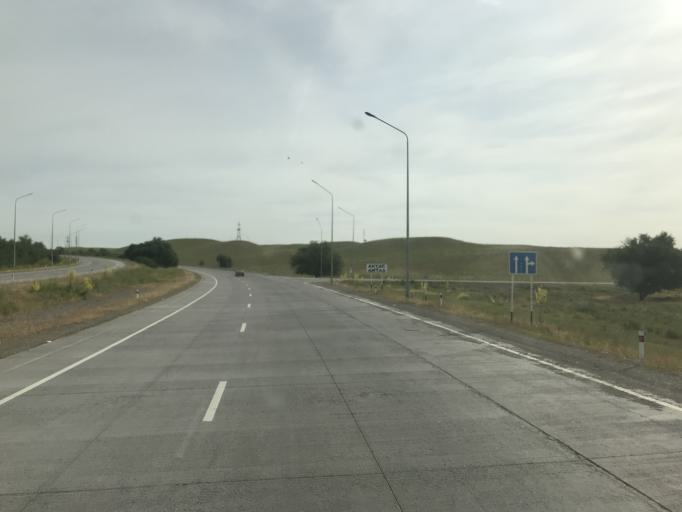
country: KZ
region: Ongtustik Qazaqstan
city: Shymkent
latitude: 42.2199
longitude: 69.5307
